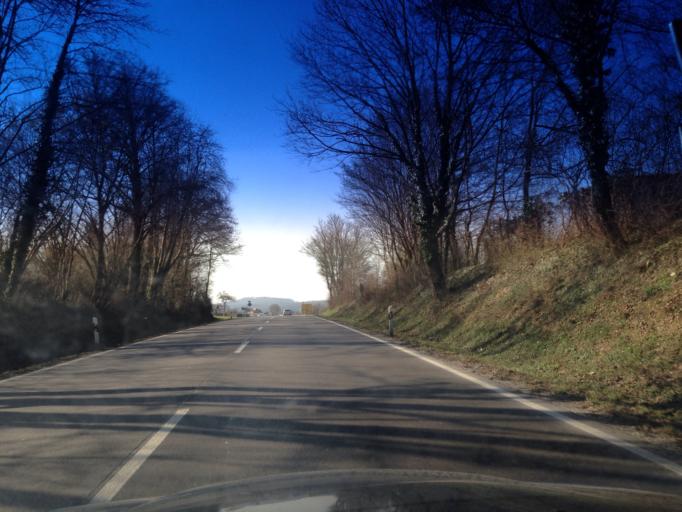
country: DE
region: Baden-Wuerttemberg
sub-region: Karlsruhe Region
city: Illingen
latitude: 48.9519
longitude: 8.9177
